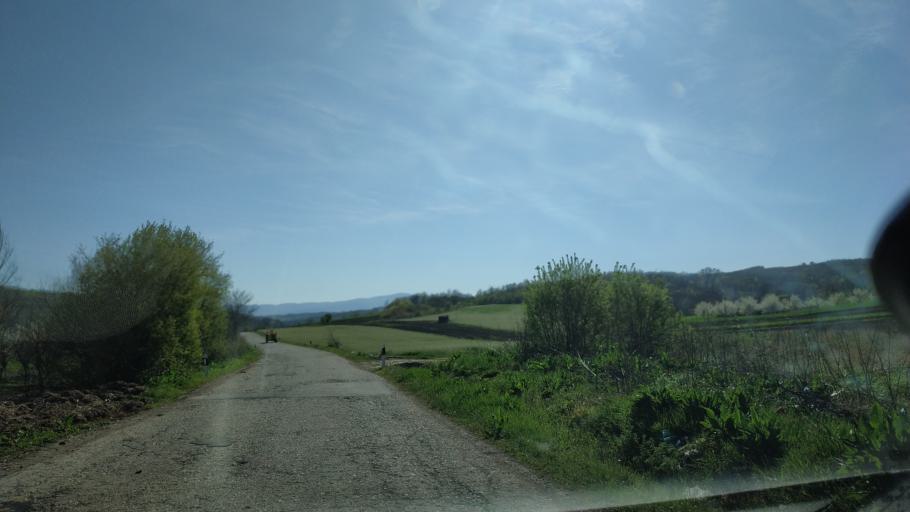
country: RS
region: Central Serbia
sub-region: Nisavski Okrug
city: Aleksinac
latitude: 43.4950
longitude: 21.6729
